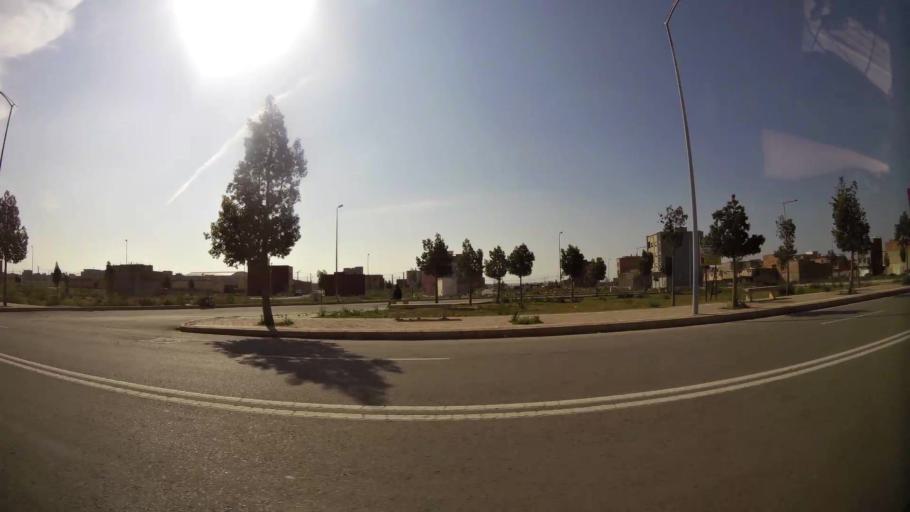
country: MA
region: Oriental
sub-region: Oujda-Angad
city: Oujda
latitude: 34.7165
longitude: -1.8834
